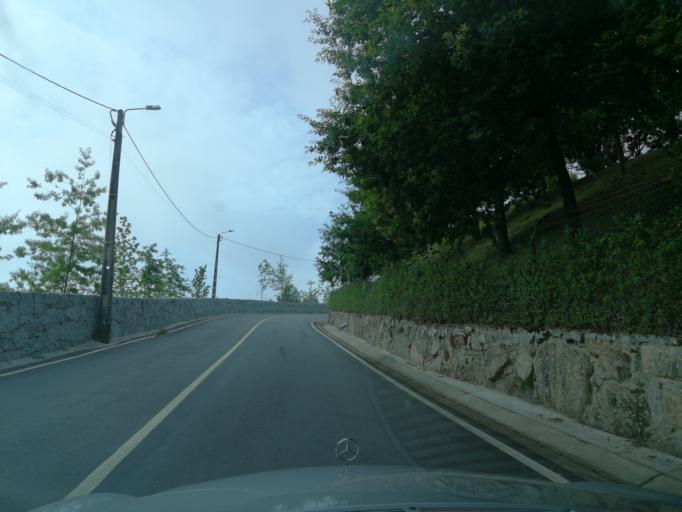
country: PT
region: Braga
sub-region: Braga
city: Braga
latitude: 41.5175
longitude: -8.3713
